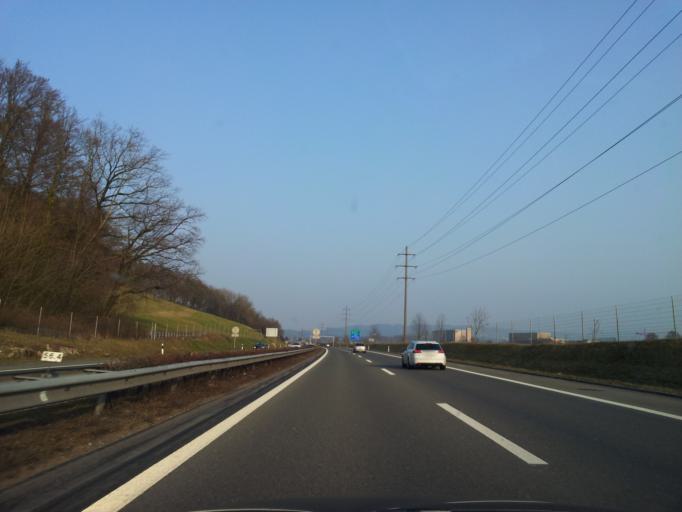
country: CH
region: Aargau
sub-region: Bezirk Brugg
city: Hausen
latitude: 47.4509
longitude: 8.2011
